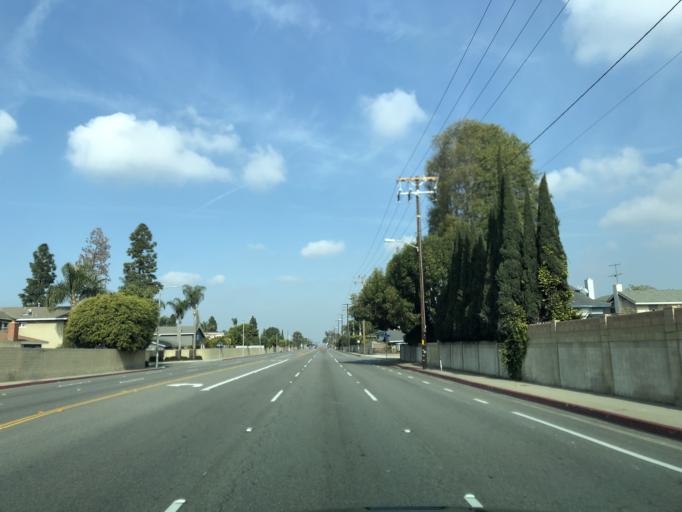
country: US
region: California
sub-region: Orange County
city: Midway City
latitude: 33.7235
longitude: -118.0067
